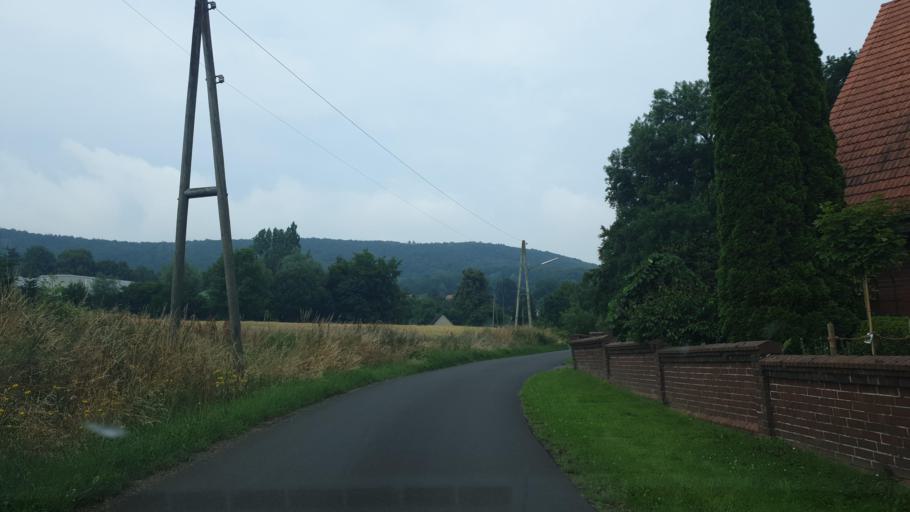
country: DE
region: North Rhine-Westphalia
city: Bad Oeynhausen
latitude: 52.2540
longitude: 8.7900
